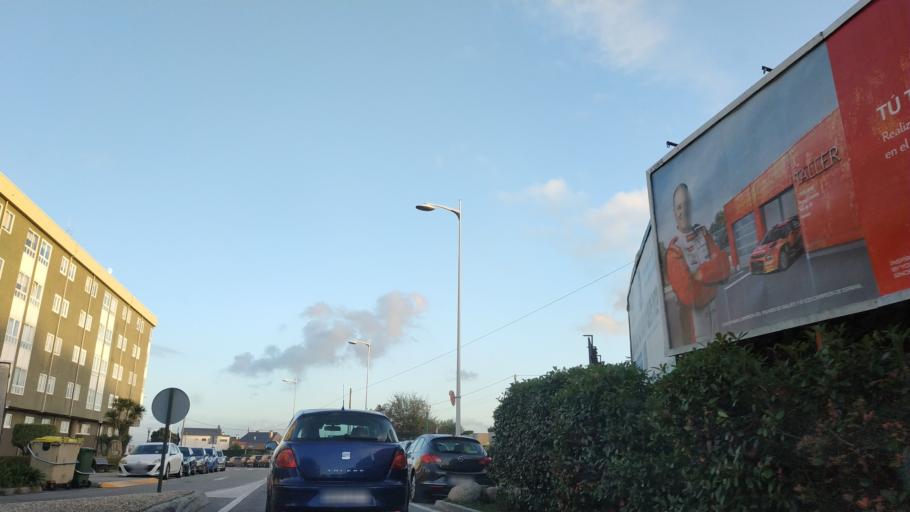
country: ES
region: Galicia
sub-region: Provincia da Coruna
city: A Coruna
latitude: 43.3597
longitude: -8.4267
